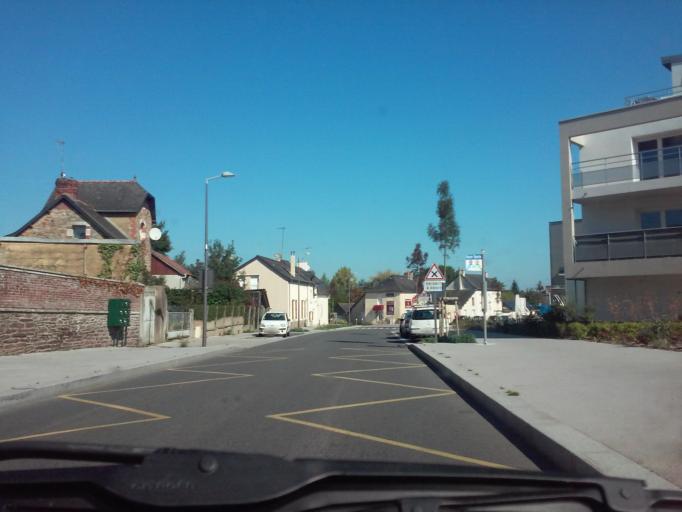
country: FR
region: Brittany
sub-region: Departement d'Ille-et-Vilaine
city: Saint-Gregoire
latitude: 48.1491
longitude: -1.6565
